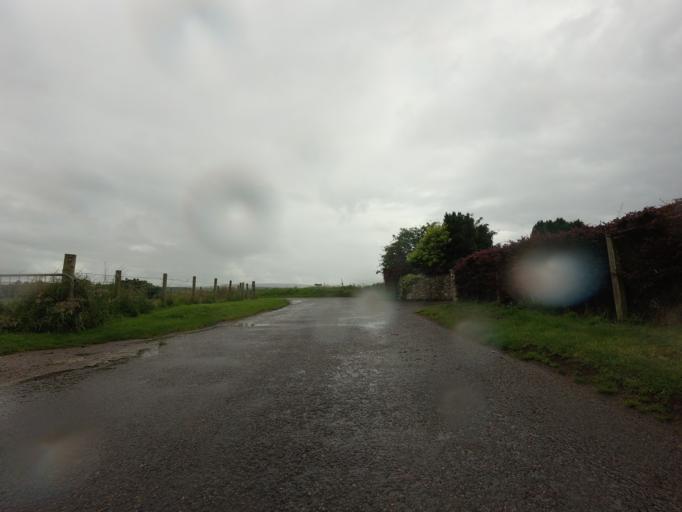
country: GB
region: Scotland
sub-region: Moray
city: Fochabers
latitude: 57.6594
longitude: -3.0733
